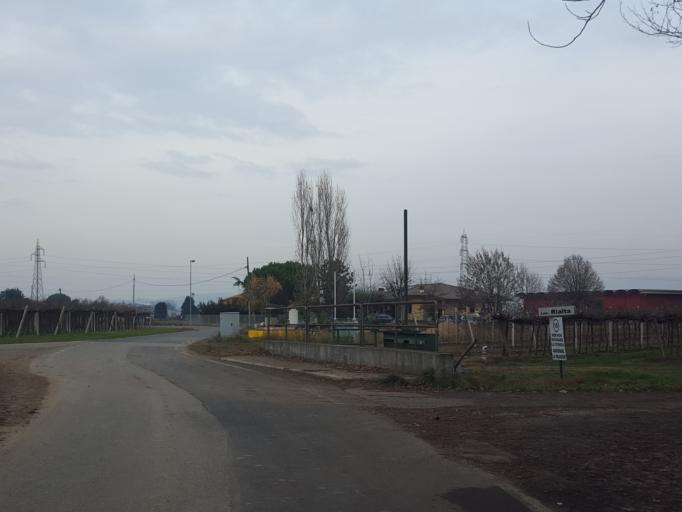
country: IT
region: Veneto
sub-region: Provincia di Verona
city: San Bonifacio
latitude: 45.3827
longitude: 11.2886
